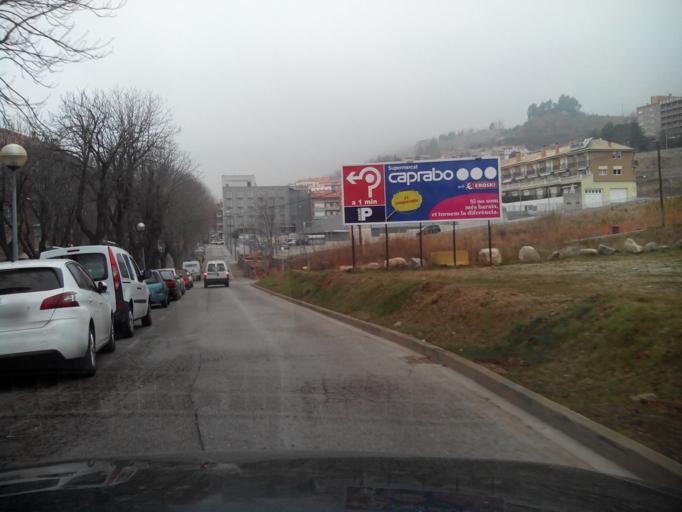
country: ES
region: Catalonia
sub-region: Provincia de Barcelona
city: Berga
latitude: 42.1048
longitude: 1.8563
